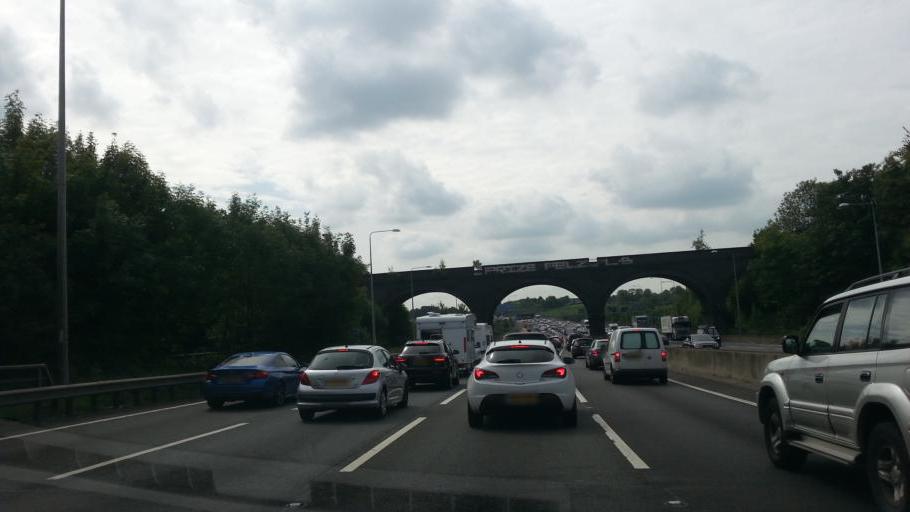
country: GB
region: England
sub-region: Buckinghamshire
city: Gerrards Cross
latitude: 51.5833
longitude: -0.5341
